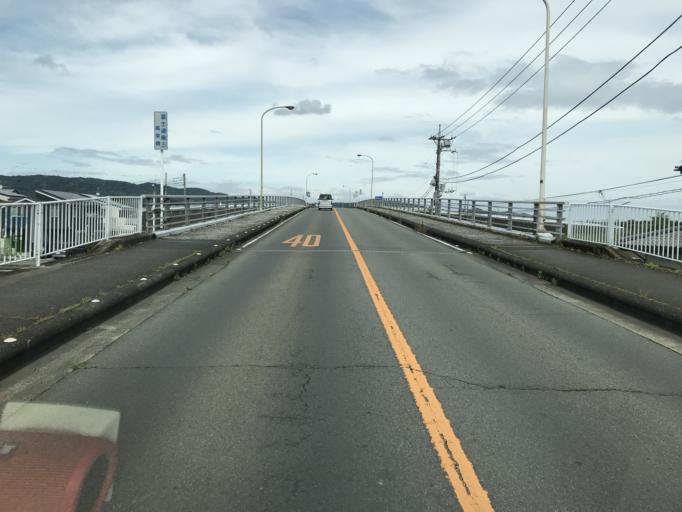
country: JP
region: Kanagawa
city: Odawara
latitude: 35.2958
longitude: 139.1533
